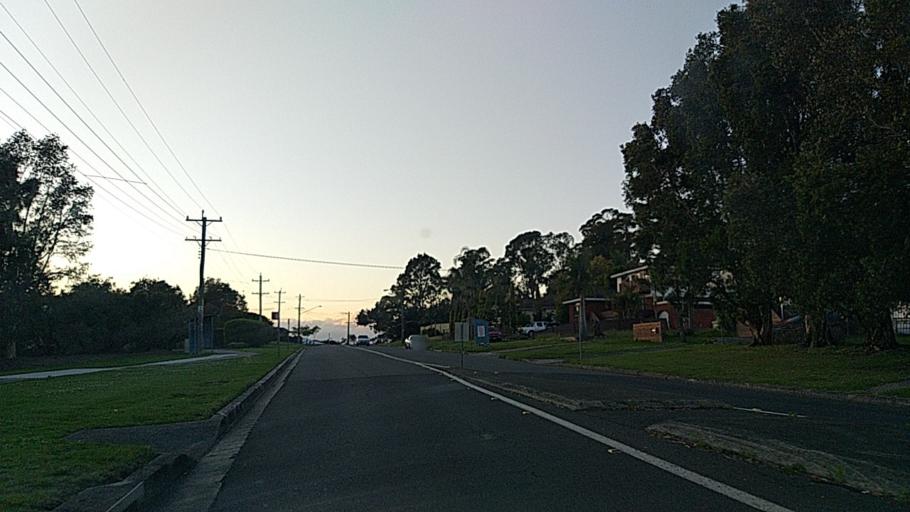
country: AU
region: New South Wales
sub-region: Wollongong
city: Koonawarra
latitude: -34.4937
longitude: 150.8176
